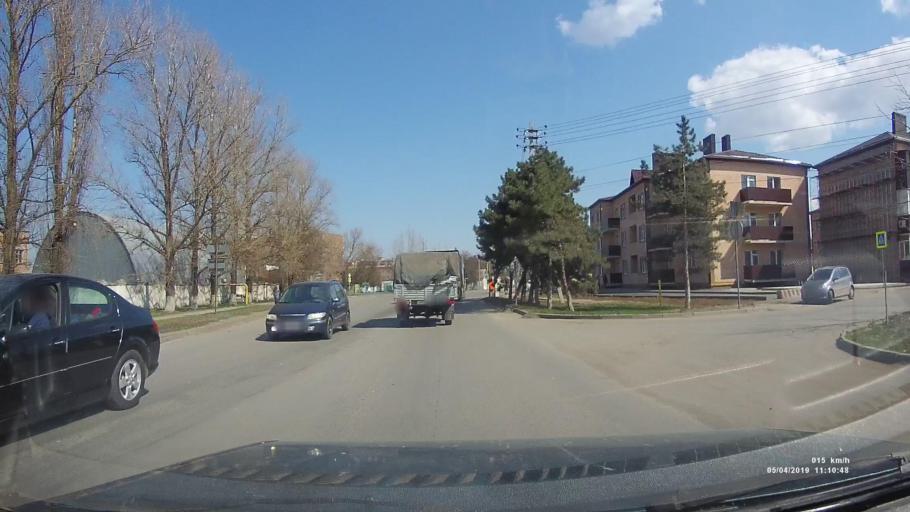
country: RU
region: Rostov
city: Azov
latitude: 47.0928
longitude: 39.4322
